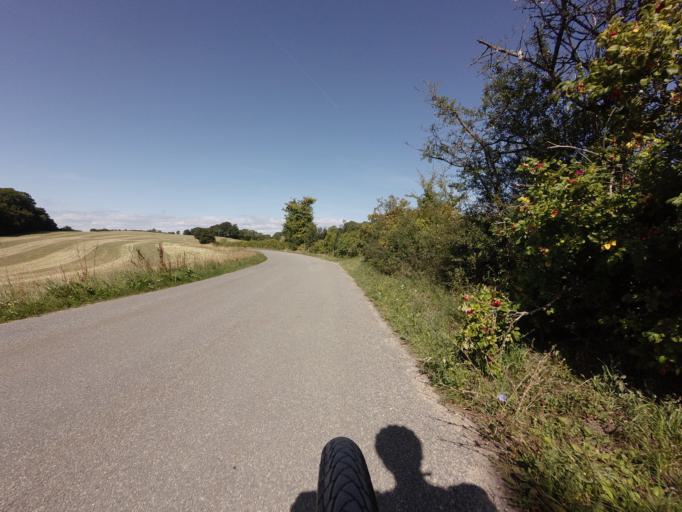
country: DK
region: Zealand
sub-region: Vordingborg Kommune
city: Stege
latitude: 54.9842
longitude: 12.5256
